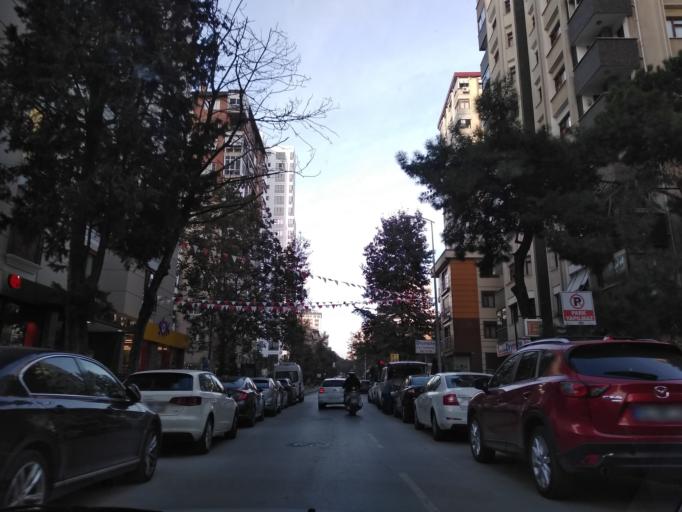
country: TR
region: Istanbul
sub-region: Atasehir
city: Atasehir
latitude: 40.9685
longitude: 29.0886
